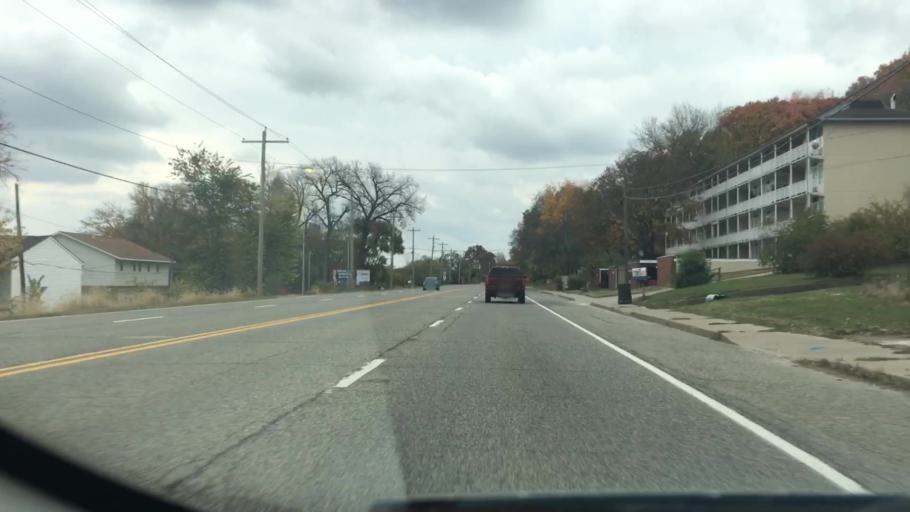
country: US
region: Illinois
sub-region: Peoria County
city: Peoria Heights
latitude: 40.7455
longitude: -89.5566
